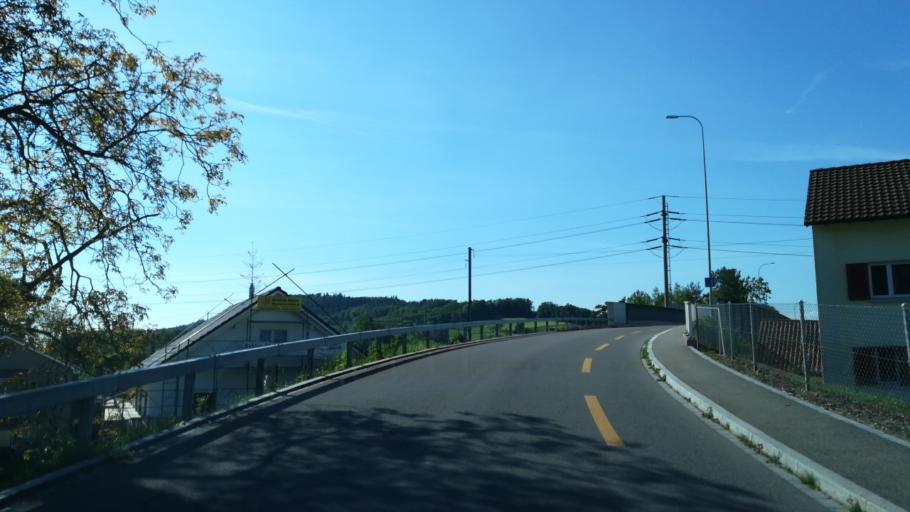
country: CH
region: Thurgau
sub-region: Frauenfeld District
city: Wagenhausen
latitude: 47.6603
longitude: 8.8167
